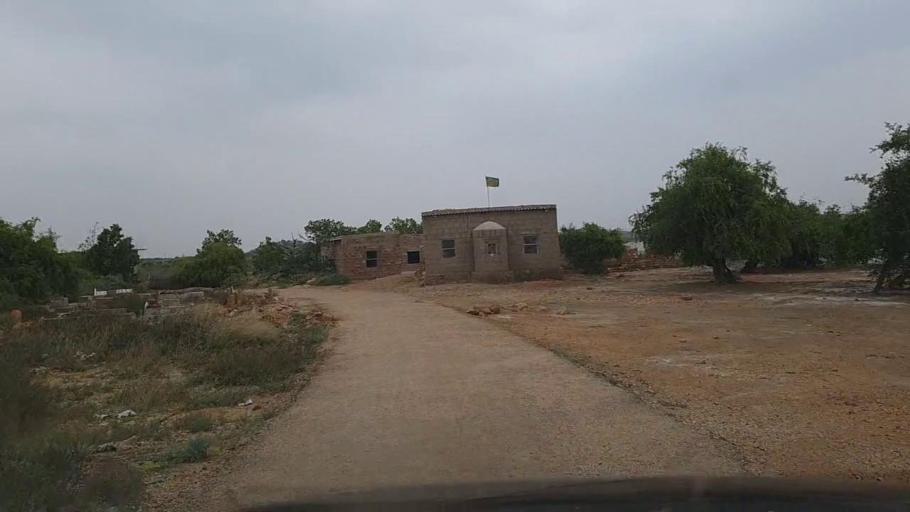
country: PK
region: Sindh
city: Thatta
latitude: 24.8174
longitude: 67.8228
